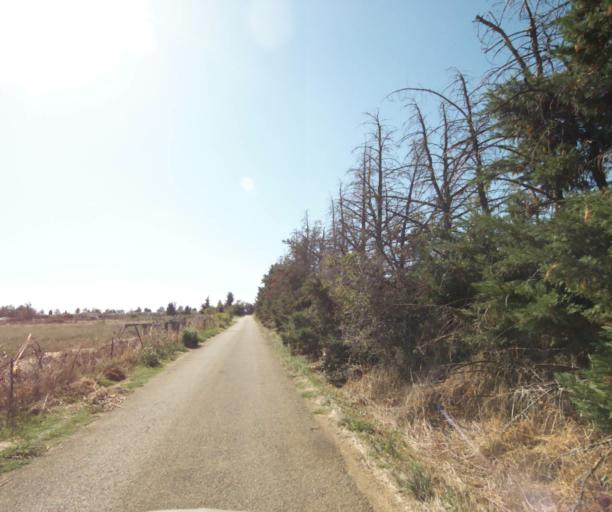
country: FR
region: Languedoc-Roussillon
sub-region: Departement du Gard
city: Bouillargues
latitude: 43.8055
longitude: 4.4414
